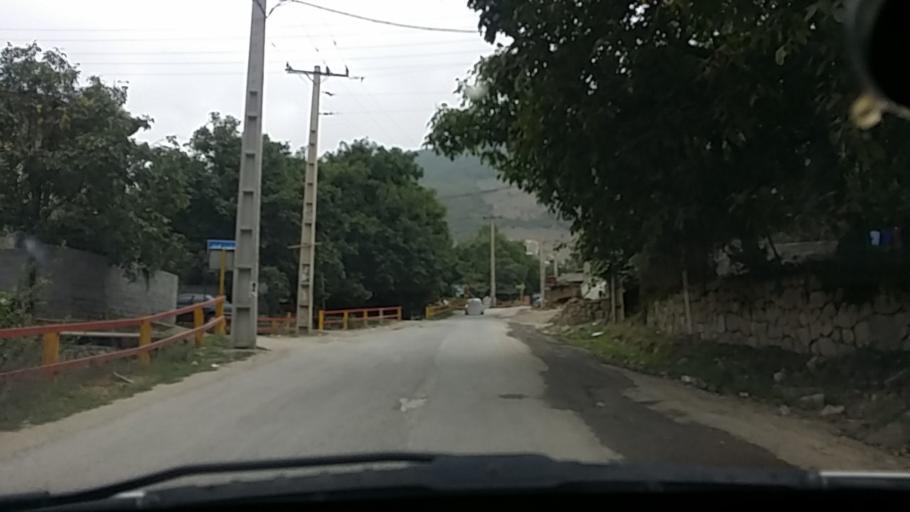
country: IR
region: Mazandaran
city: `Abbasabad
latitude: 36.4849
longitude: 51.1341
